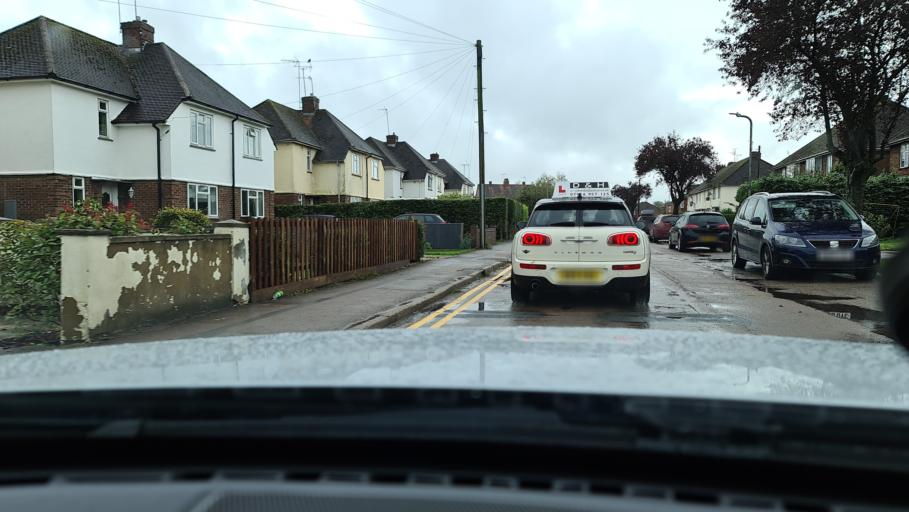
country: GB
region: England
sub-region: Buckinghamshire
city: Bletchley
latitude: 51.9992
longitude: -0.7288
